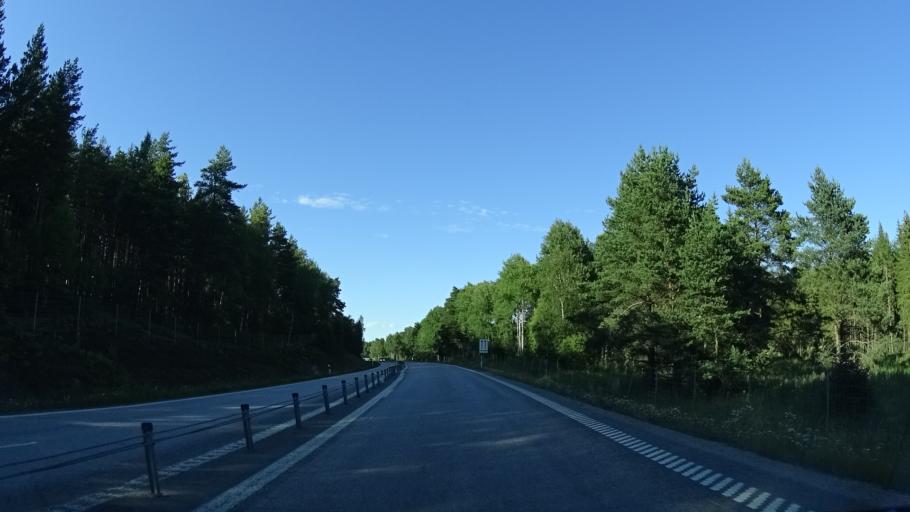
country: SE
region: Stockholm
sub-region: Vallentuna Kommun
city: Vallentuna
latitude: 59.5247
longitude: 18.1872
